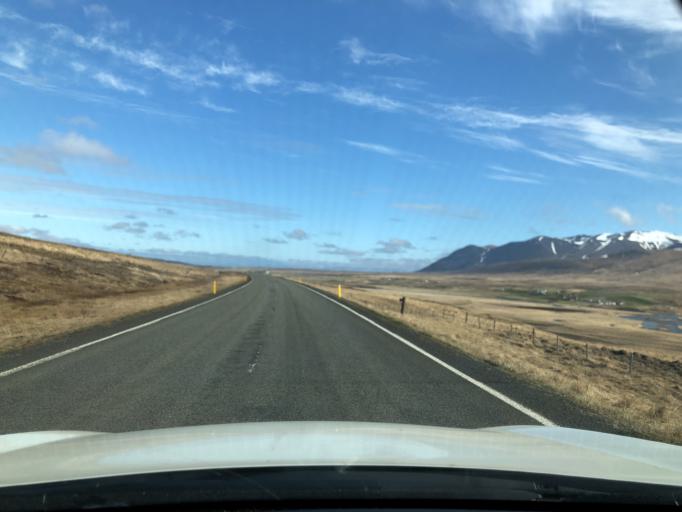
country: IS
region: Northwest
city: Saudarkrokur
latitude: 65.3680
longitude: -20.6481
